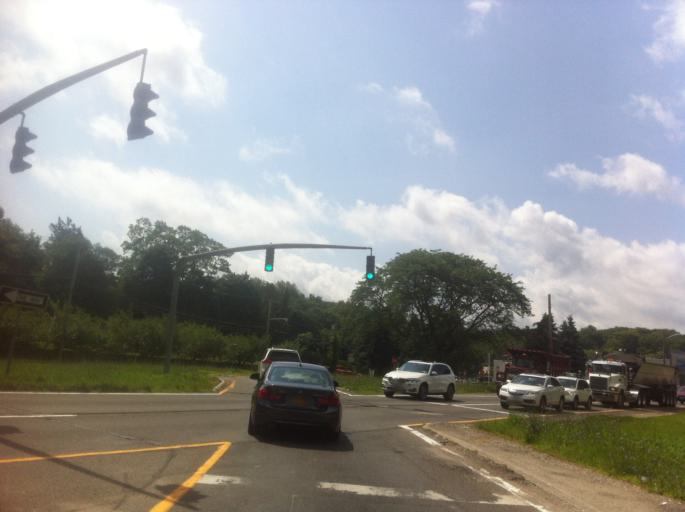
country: US
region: New York
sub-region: Nassau County
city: Glen Head
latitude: 40.8399
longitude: -73.6151
